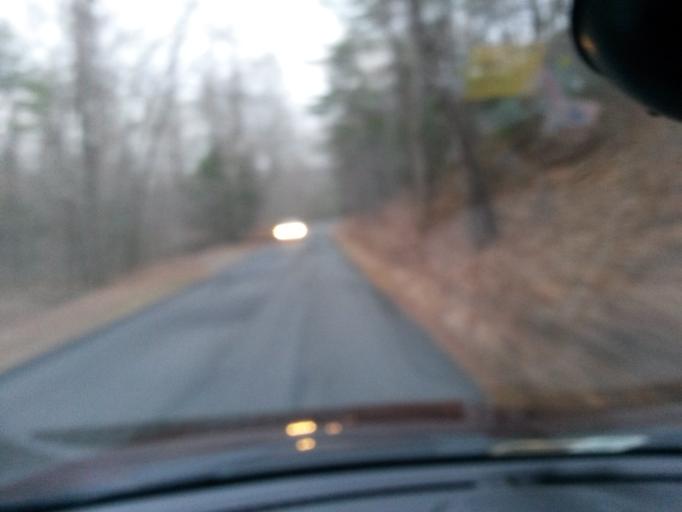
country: US
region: Virginia
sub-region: Bath County
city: Warm Springs
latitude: 37.9373
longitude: -79.7825
